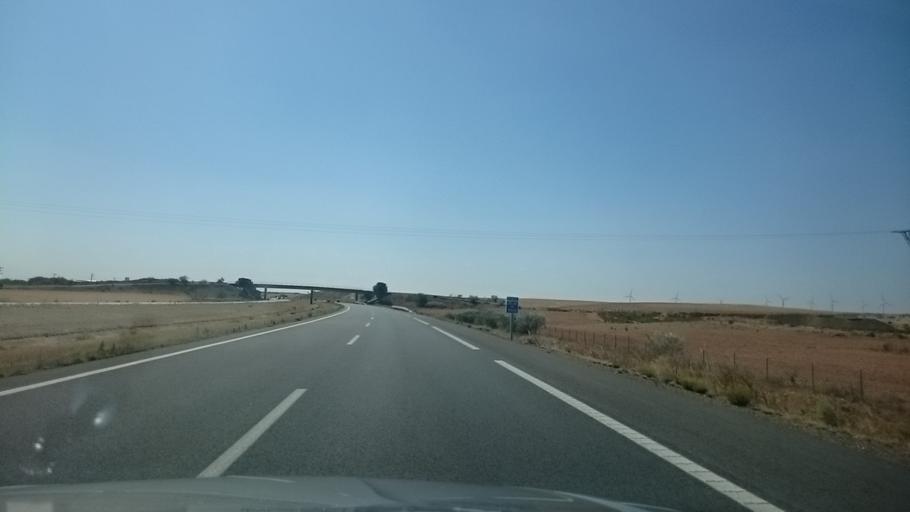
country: ES
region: Aragon
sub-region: Provincia de Zaragoza
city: Luceni
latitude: 41.7912
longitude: -1.2563
